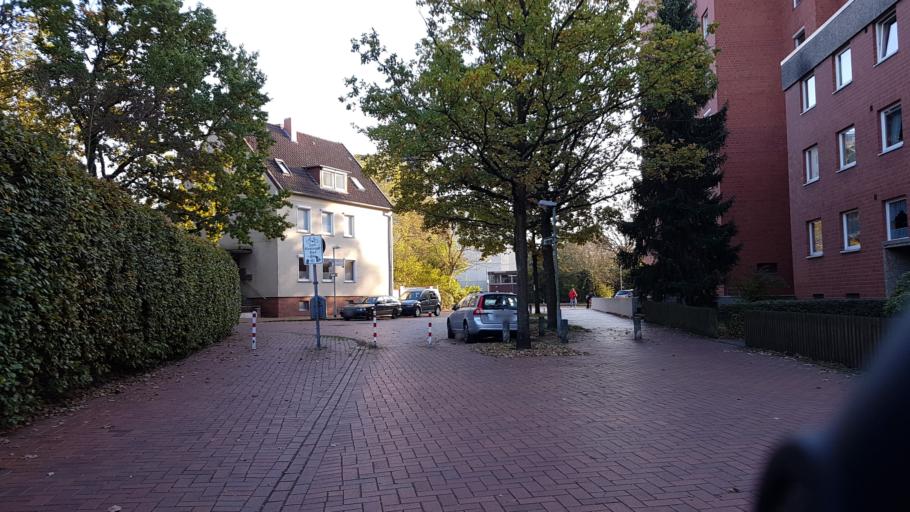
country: DE
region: Lower Saxony
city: Hemmingen
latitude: 52.3417
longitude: 9.7289
